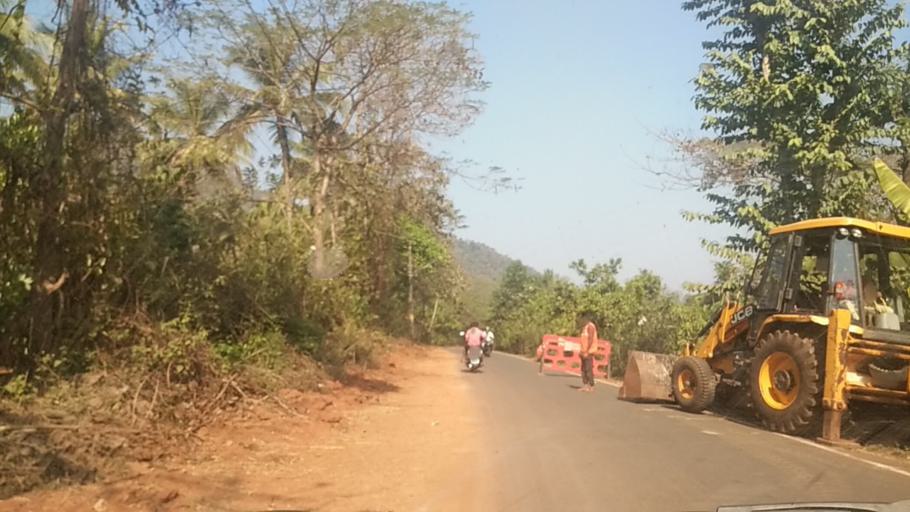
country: IN
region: Goa
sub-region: South Goa
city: Sanguem
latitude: 15.1860
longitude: 74.2270
